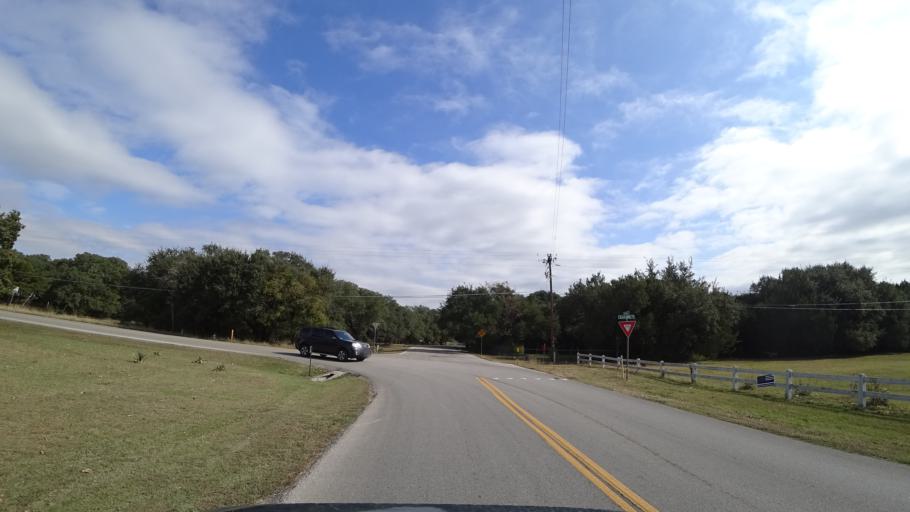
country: US
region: Texas
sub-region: Williamson County
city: Brushy Creek
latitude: 30.5241
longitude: -97.7361
